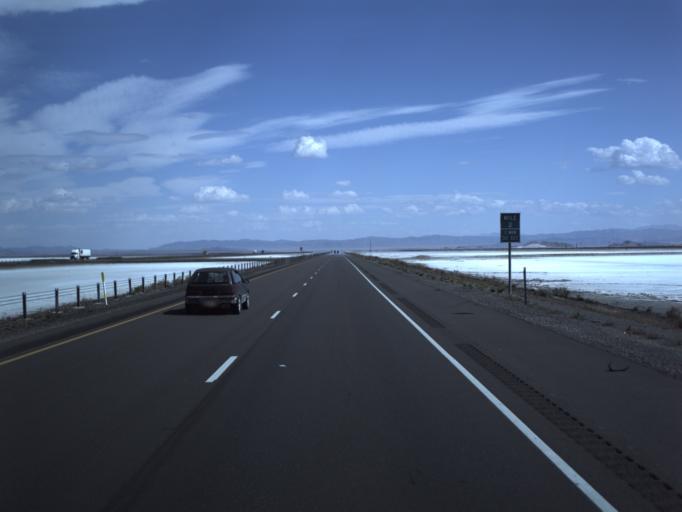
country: US
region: Utah
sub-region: Tooele County
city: Wendover
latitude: 40.7287
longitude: -113.4079
